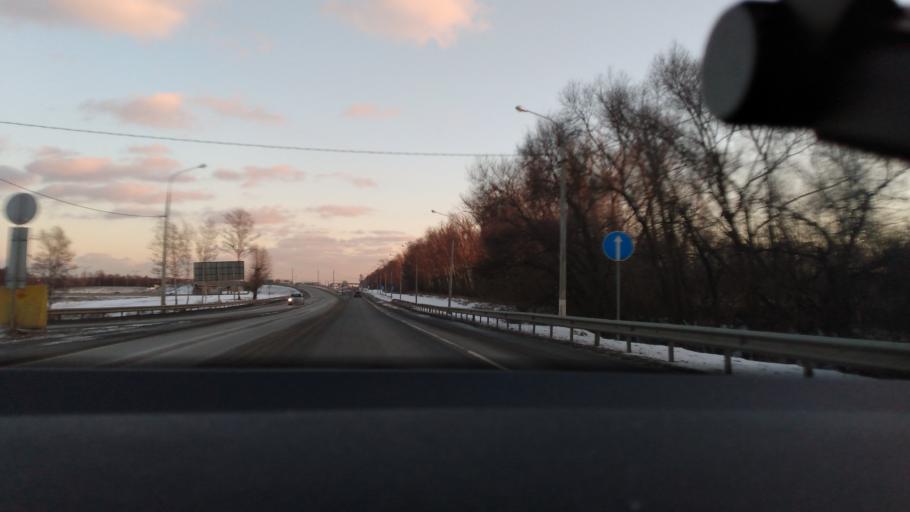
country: RU
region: Moskovskaya
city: Raduzhnyy
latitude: 55.1680
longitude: 38.6694
